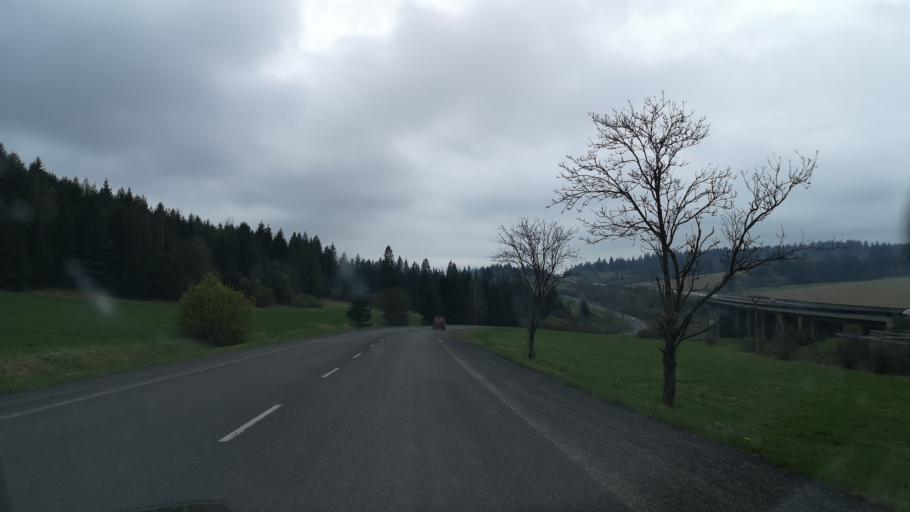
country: SK
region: Zilinsky
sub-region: Okres Liptovsky Mikulas
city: Hybe
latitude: 49.0634
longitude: 19.9508
